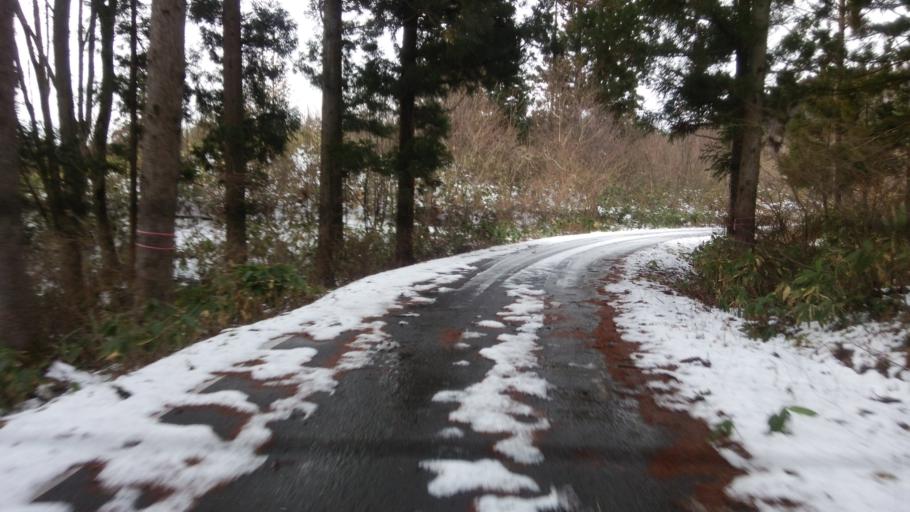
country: JP
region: Fukushima
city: Inawashiro
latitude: 37.5743
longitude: 139.9942
